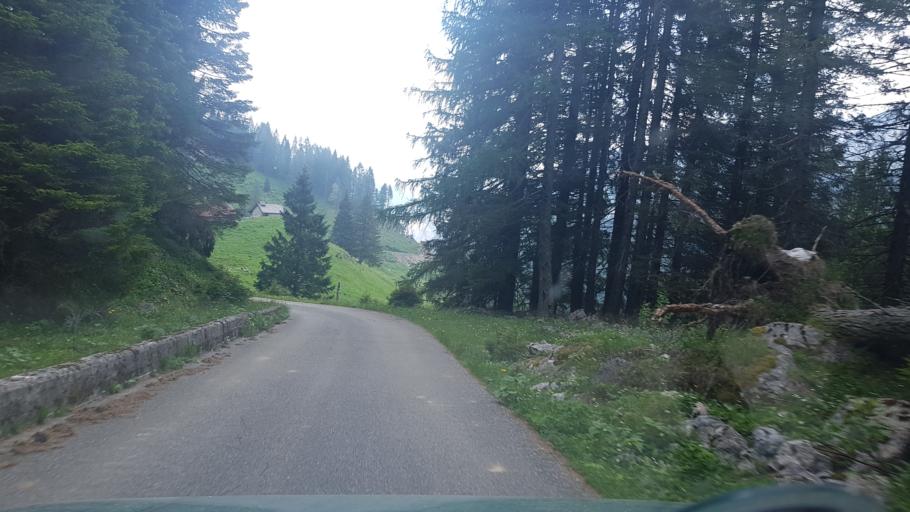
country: IT
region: Friuli Venezia Giulia
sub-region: Provincia di Udine
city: Paularo
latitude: 46.5565
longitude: 13.1886
